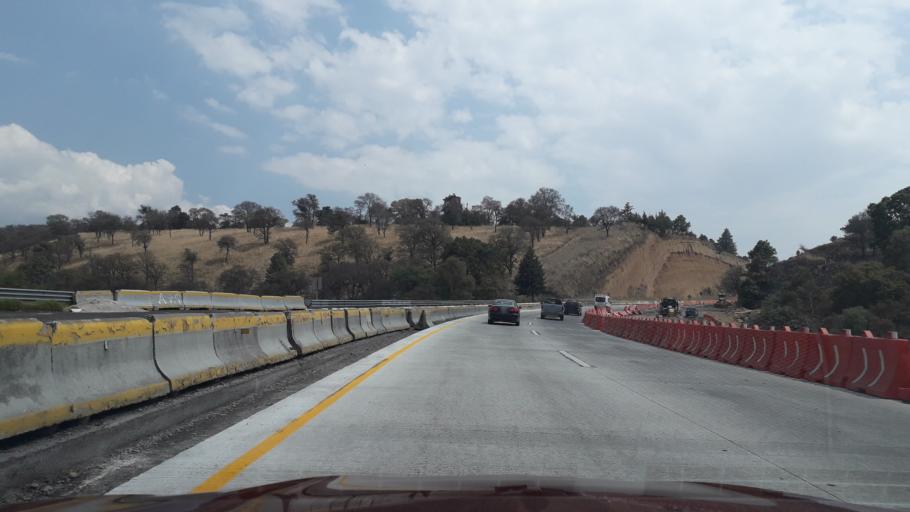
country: MX
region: Mexico
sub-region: Ixtapaluca
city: San Jeronimo Cuatro Vientos
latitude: 19.3114
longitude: -98.7931
